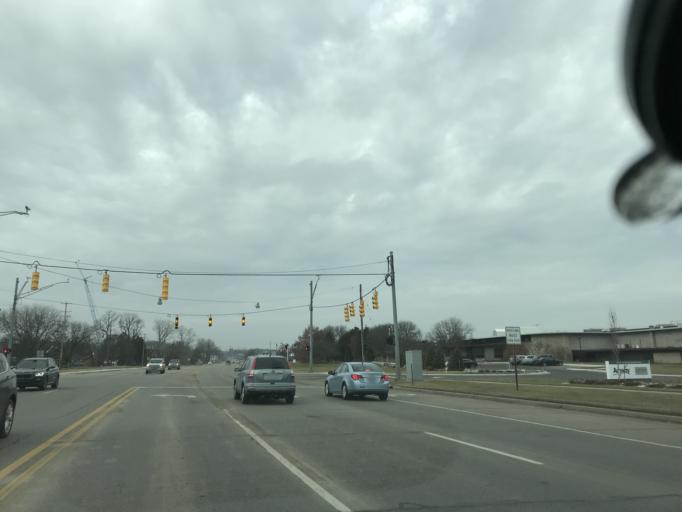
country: US
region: Michigan
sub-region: Kent County
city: Forest Hills
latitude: 42.9558
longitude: -85.4829
